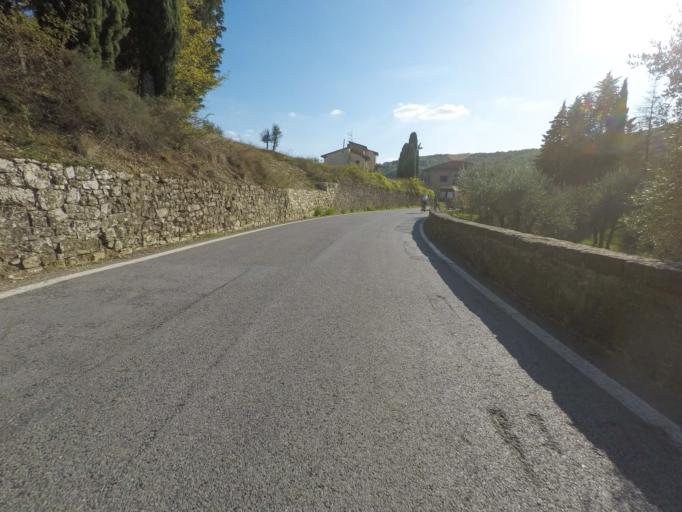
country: IT
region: Tuscany
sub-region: Provincia di Siena
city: Radda in Chianti
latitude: 43.4854
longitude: 11.3698
